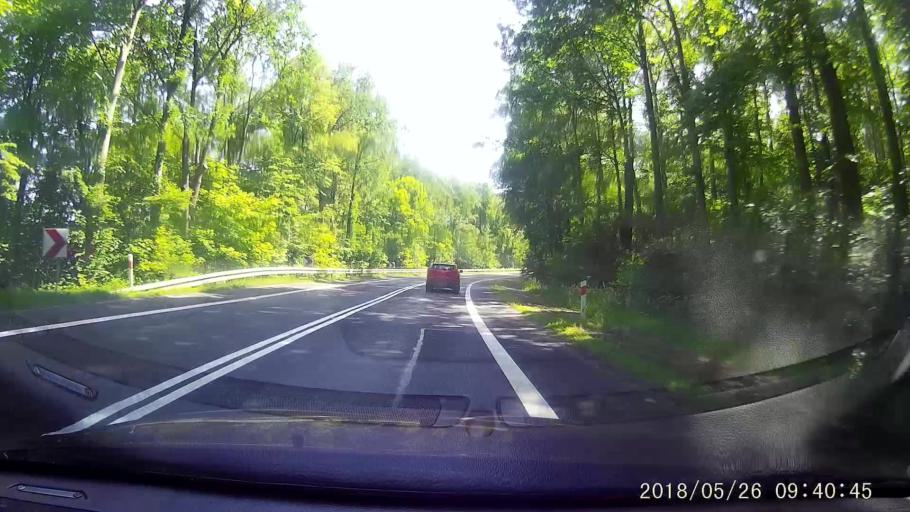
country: PL
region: Lower Silesian Voivodeship
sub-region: Powiat lubanski
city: Siekierczyn
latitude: 51.1630
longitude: 15.1409
